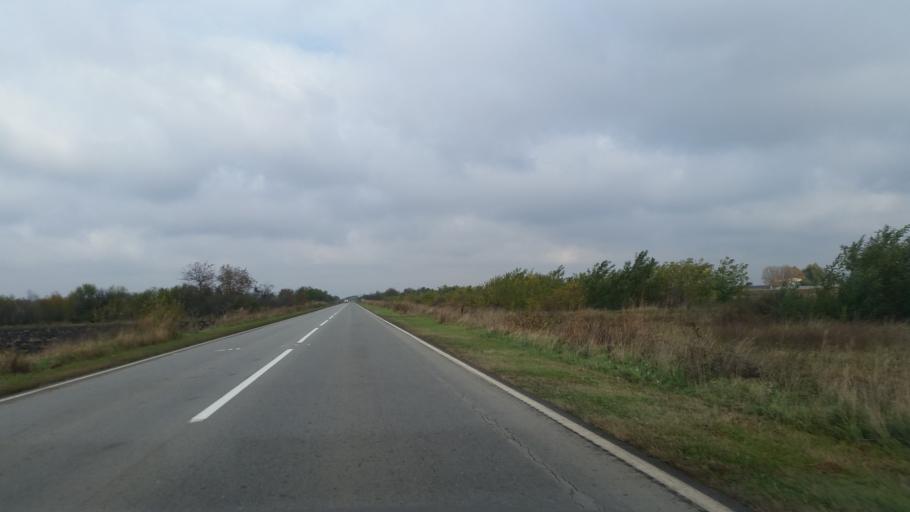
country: RS
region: Autonomna Pokrajina Vojvodina
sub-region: Srednjebanatski Okrug
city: Zrenjanin
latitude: 45.4283
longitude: 20.3696
